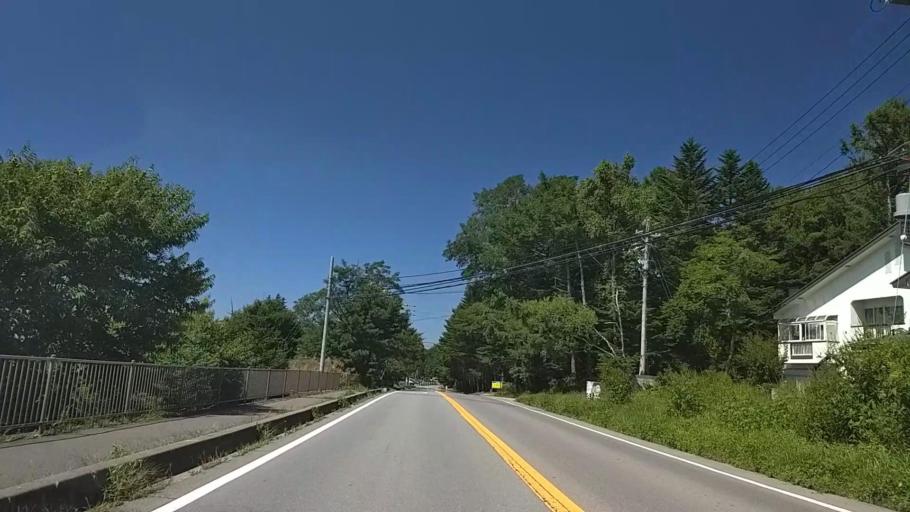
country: JP
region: Nagano
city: Komoro
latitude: 36.3355
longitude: 138.5122
